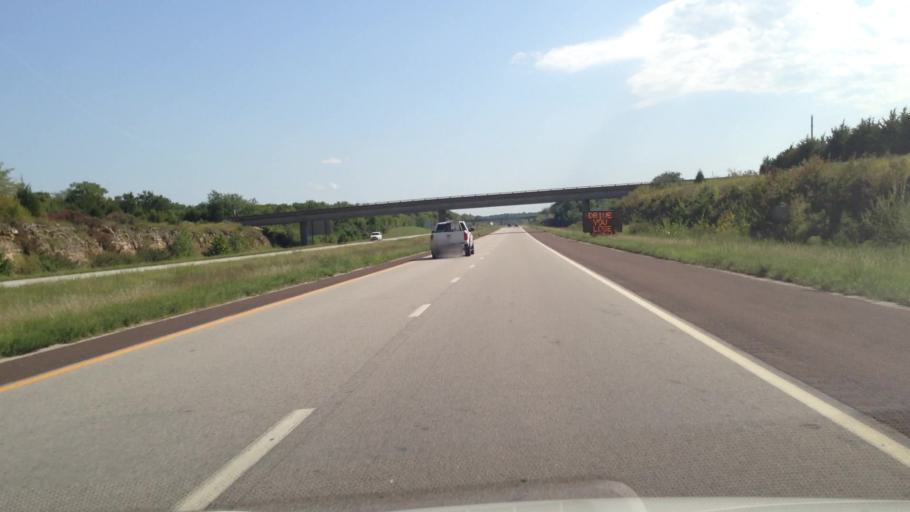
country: US
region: Kansas
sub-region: Miami County
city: Louisburg
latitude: 38.6155
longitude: -94.6950
